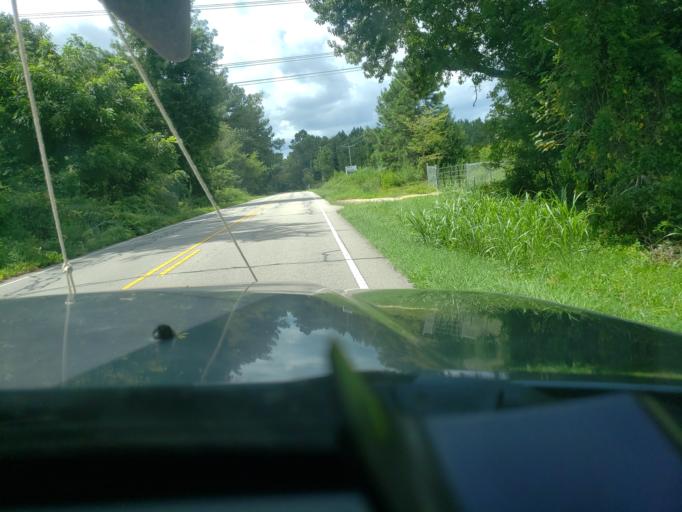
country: US
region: North Carolina
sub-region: Wake County
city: Rolesville
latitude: 35.8786
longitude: -78.4672
